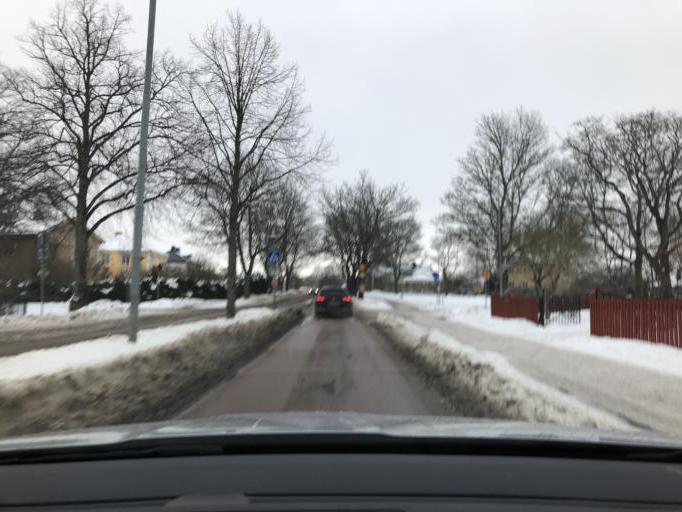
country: SE
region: Uppsala
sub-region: Uppsala Kommun
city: Uppsala
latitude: 59.8465
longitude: 17.6255
